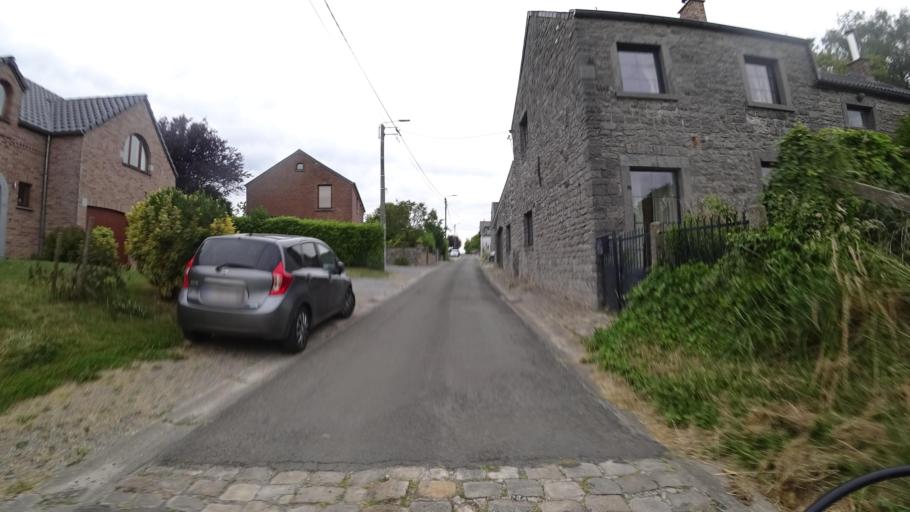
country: BE
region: Wallonia
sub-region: Province de Namur
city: Namur
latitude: 50.5206
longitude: 4.8425
